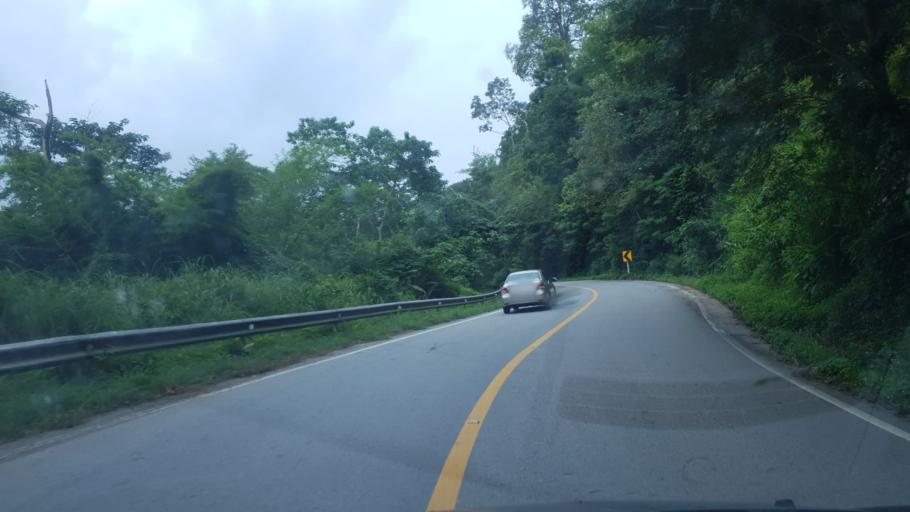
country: TH
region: Mae Hong Son
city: Khun Yuam
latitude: 18.7082
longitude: 97.9116
